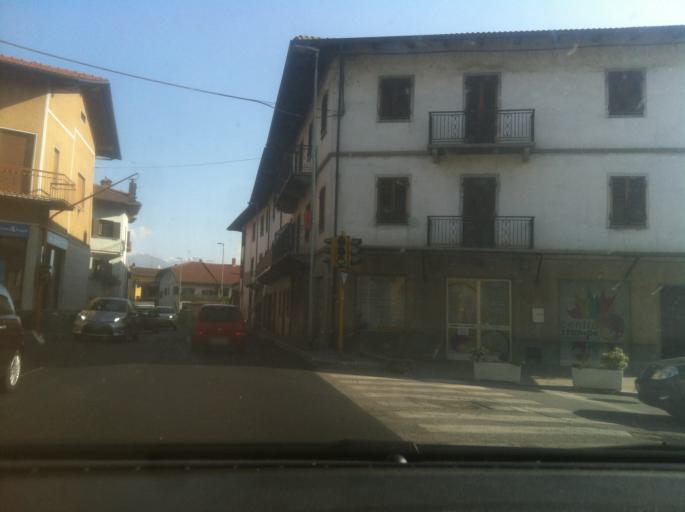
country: IT
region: Piedmont
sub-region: Provincia di Torino
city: Strambino
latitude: 45.3835
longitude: 7.8854
